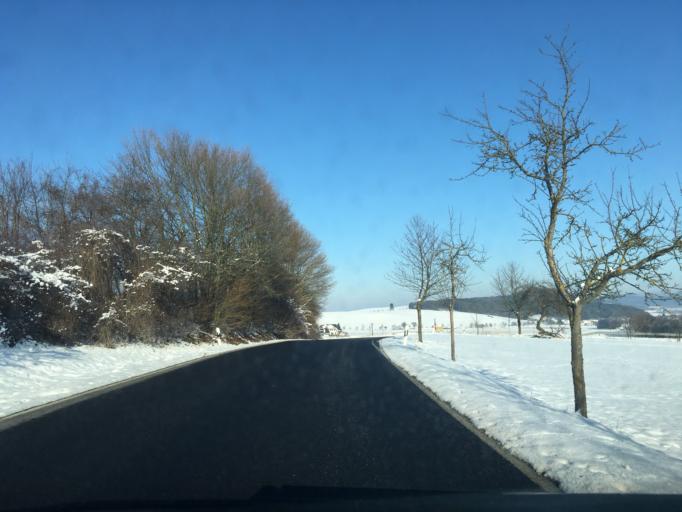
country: DE
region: Thuringia
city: Schleid
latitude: 50.6434
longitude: 9.9313
